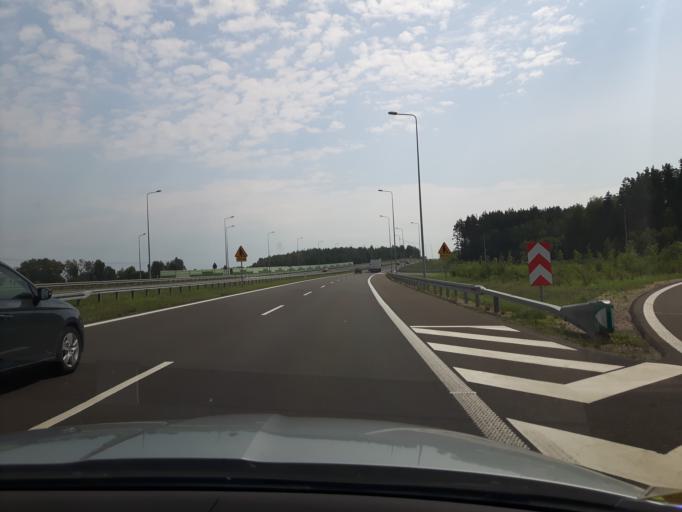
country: PL
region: Warmian-Masurian Voivodeship
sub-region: Powiat nidzicki
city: Nidzica
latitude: 53.3727
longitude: 20.3834
